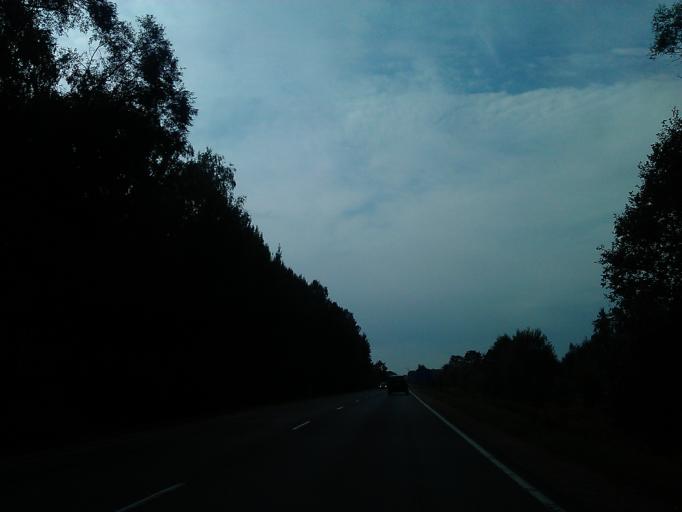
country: LV
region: Salaspils
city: Salaspils
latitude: 56.9059
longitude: 24.4062
